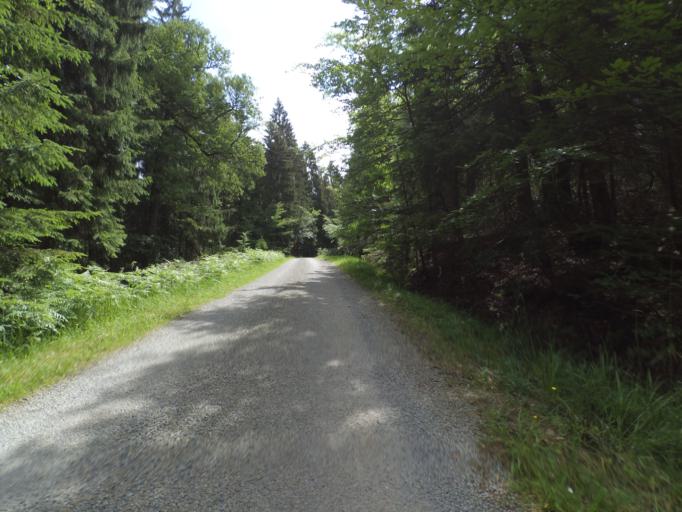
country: BE
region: Wallonia
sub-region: Province de Liege
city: Raeren
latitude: 50.6003
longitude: 6.1209
